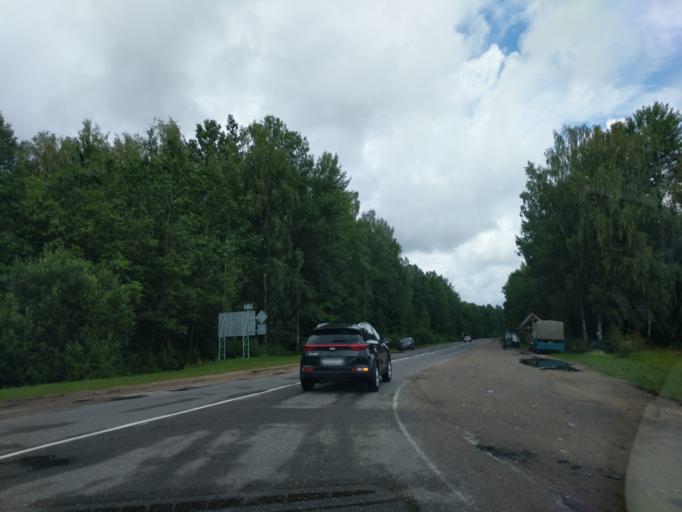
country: BY
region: Minsk
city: Il'ya
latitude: 54.4121
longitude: 27.2636
